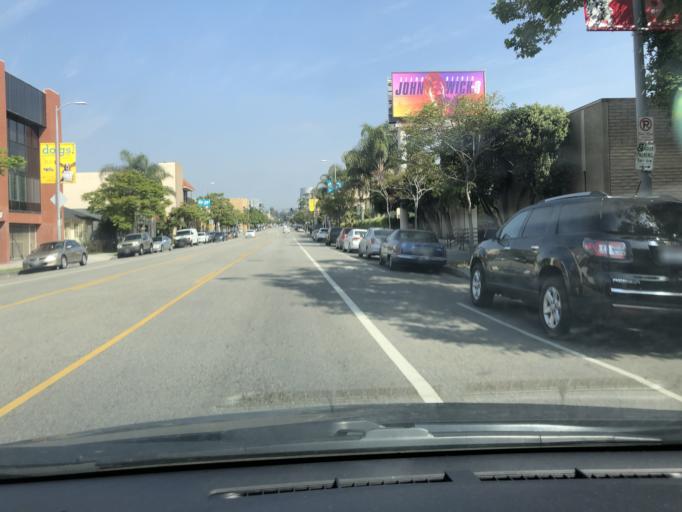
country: US
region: California
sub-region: Los Angeles County
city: Culver City
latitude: 34.0238
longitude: -118.4065
